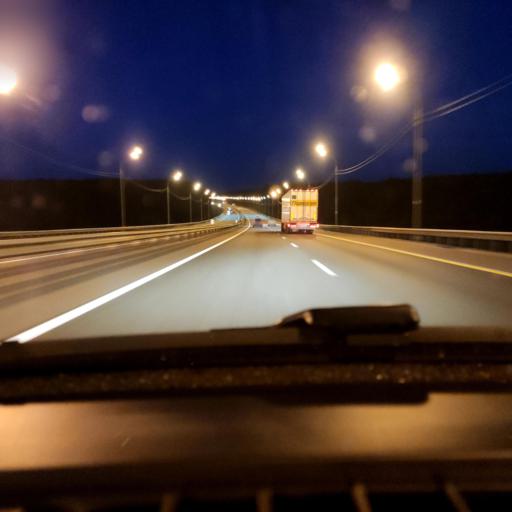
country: RU
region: Lipetsk
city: Khlevnoye
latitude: 52.2256
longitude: 39.1035
